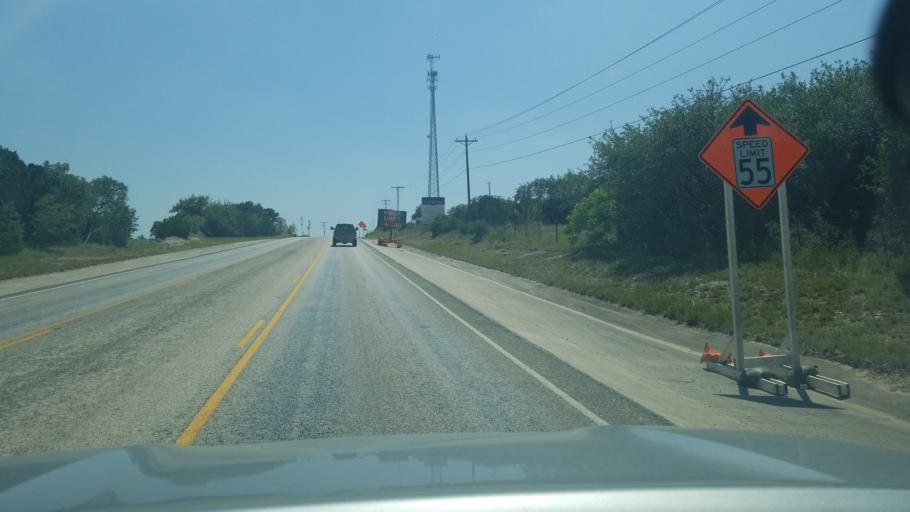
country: US
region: Texas
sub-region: Bexar County
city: Fair Oaks Ranch
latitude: 29.8242
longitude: -98.5796
